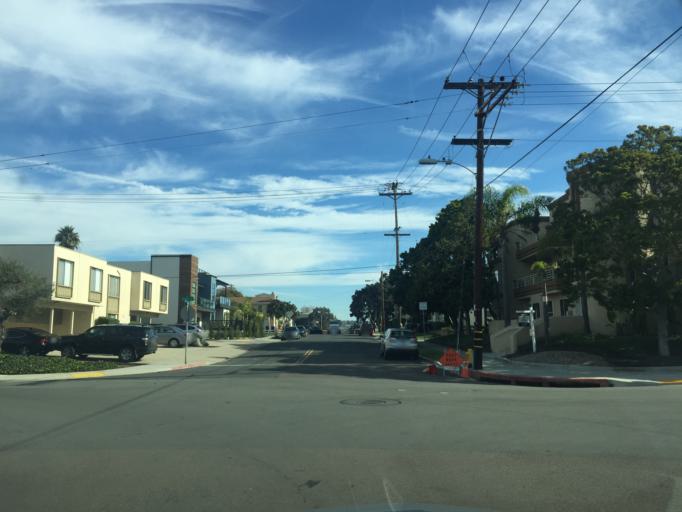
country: US
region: California
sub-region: San Diego County
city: La Jolla
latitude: 32.7891
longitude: -117.2358
